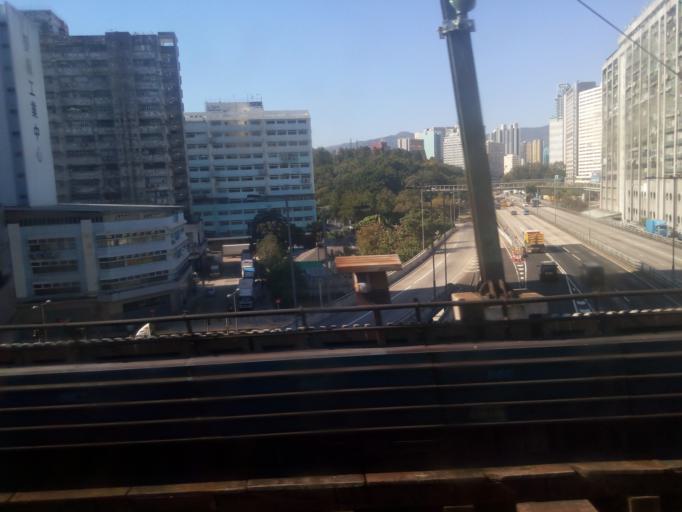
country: HK
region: Tsuen Wan
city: Tsuen Wan
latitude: 22.3535
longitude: 114.1253
